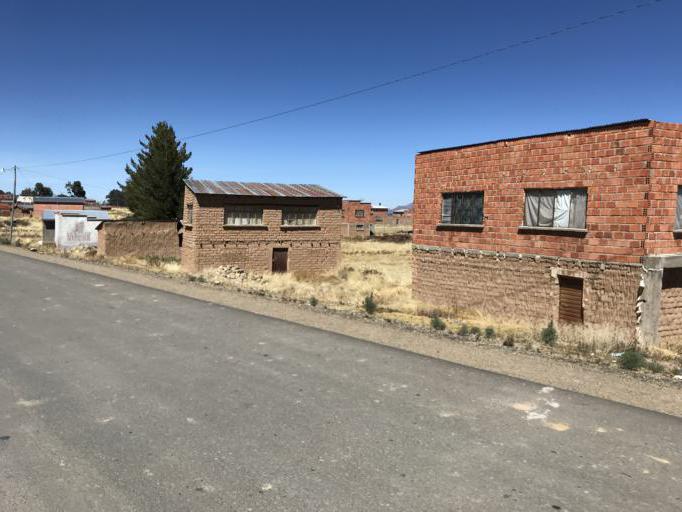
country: BO
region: La Paz
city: Huatajata
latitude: -16.1925
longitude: -68.7330
